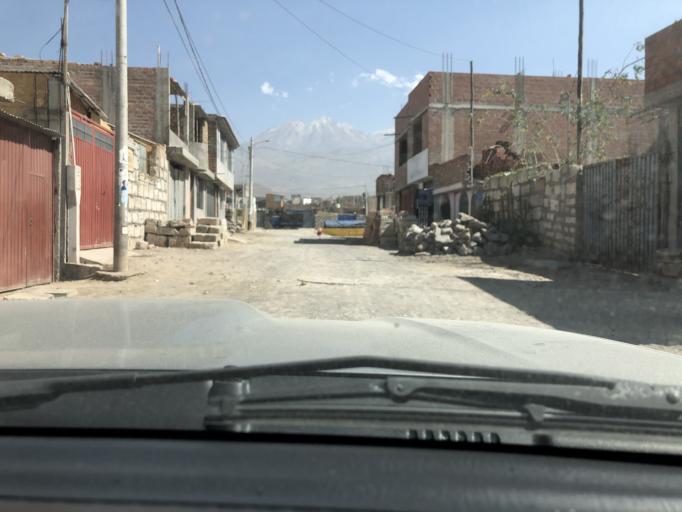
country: PE
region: Arequipa
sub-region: Provincia de Arequipa
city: Arequipa
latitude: -16.3426
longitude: -71.5511
